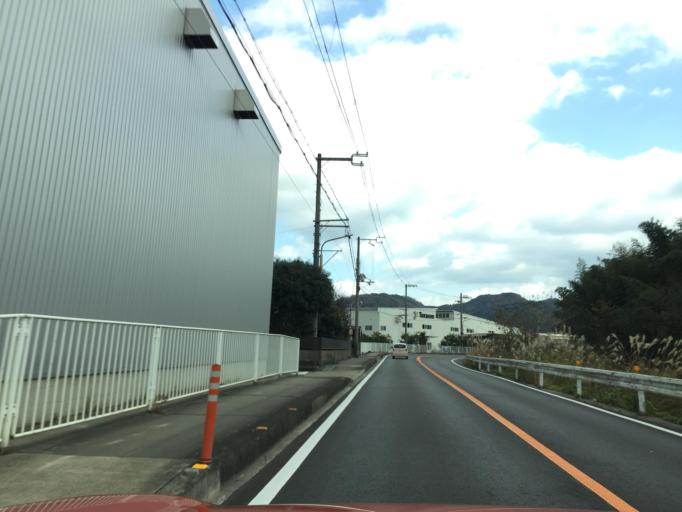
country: JP
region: Wakayama
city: Kainan
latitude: 34.1718
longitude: 135.2491
